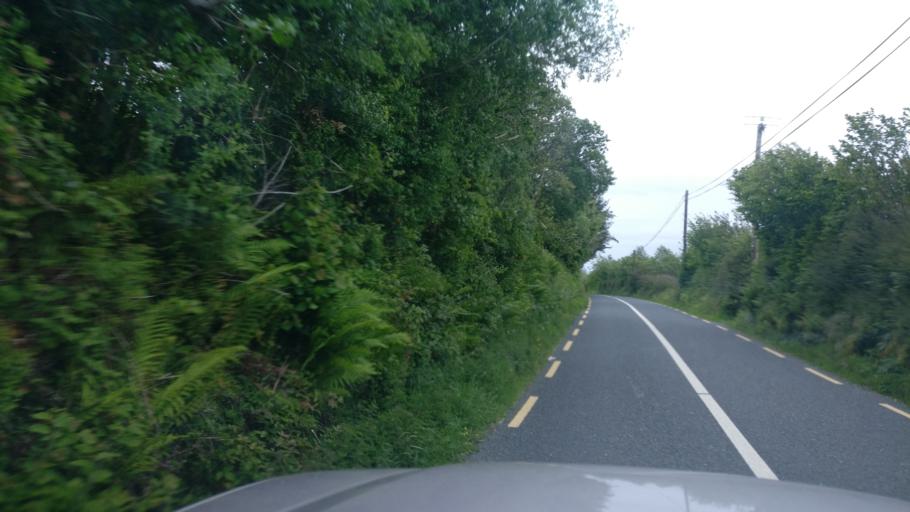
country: IE
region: Connaught
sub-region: County Galway
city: Loughrea
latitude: 53.0620
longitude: -8.6275
